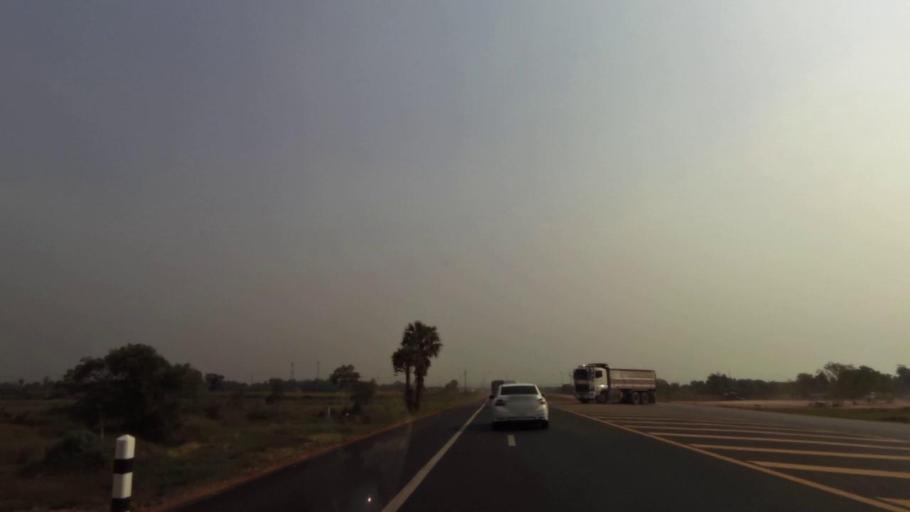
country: TH
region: Rayong
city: Klaeng
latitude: 12.7909
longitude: 101.6751
